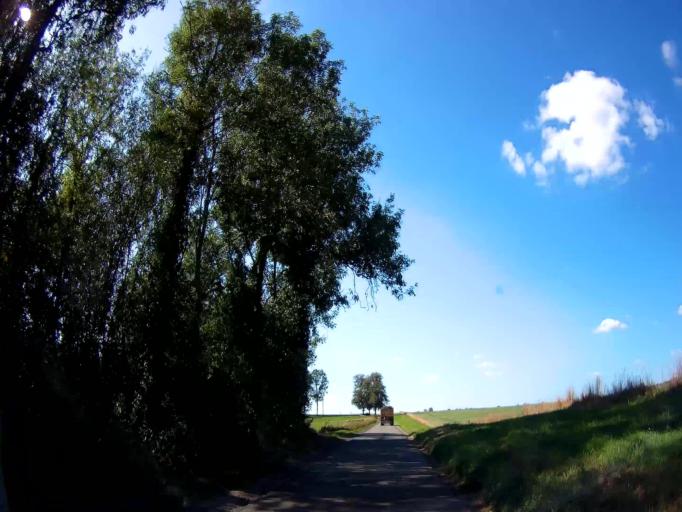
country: BE
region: Wallonia
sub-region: Province de Namur
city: Houyet
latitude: 50.2348
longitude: 4.9716
